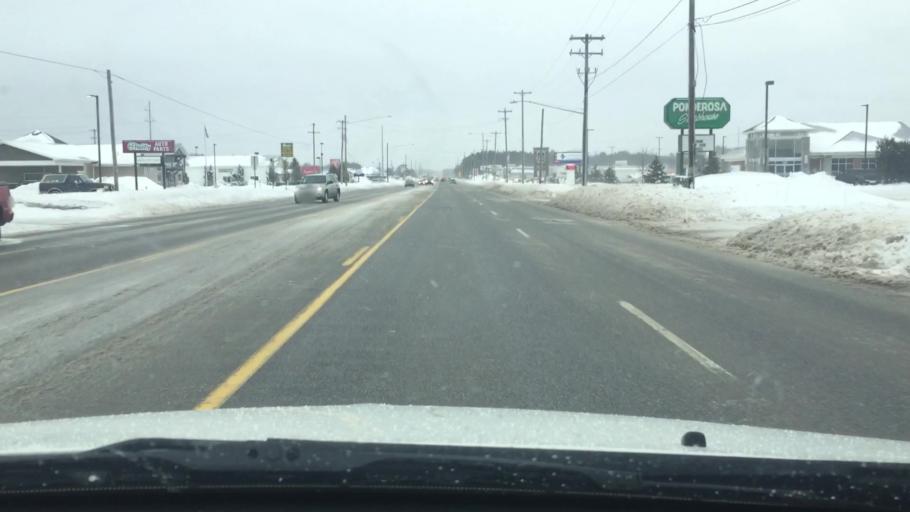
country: US
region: Michigan
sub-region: Otsego County
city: Gaylord
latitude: 45.0275
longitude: -84.6959
